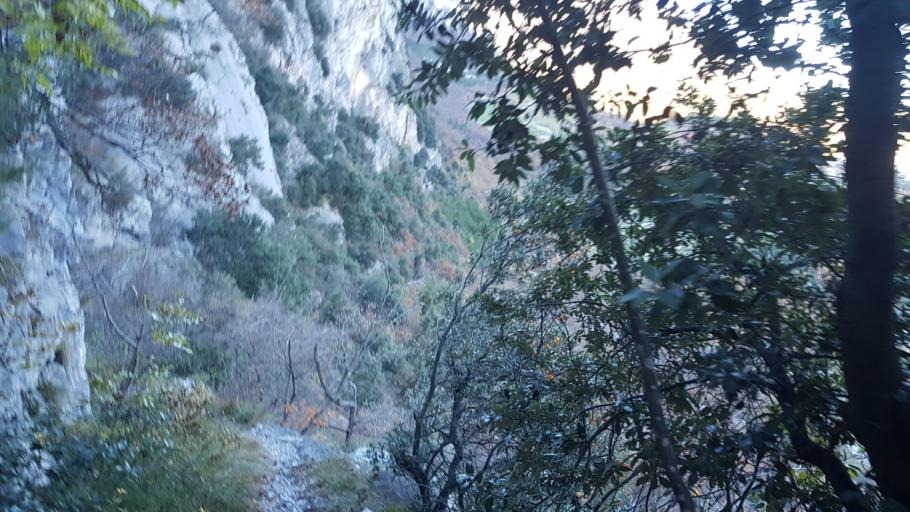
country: IT
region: Trentino-Alto Adige
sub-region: Provincia di Trento
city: Padergnone
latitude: 46.0728
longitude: 10.9800
